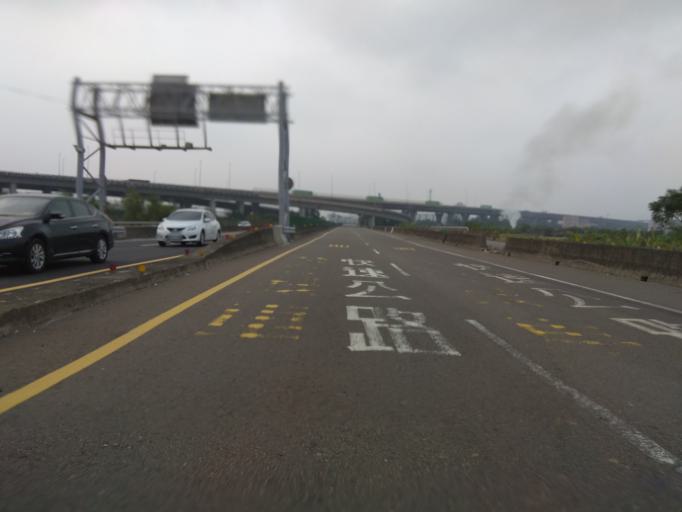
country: TW
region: Taiwan
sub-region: Hsinchu
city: Hsinchu
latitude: 24.7039
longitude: 120.8673
